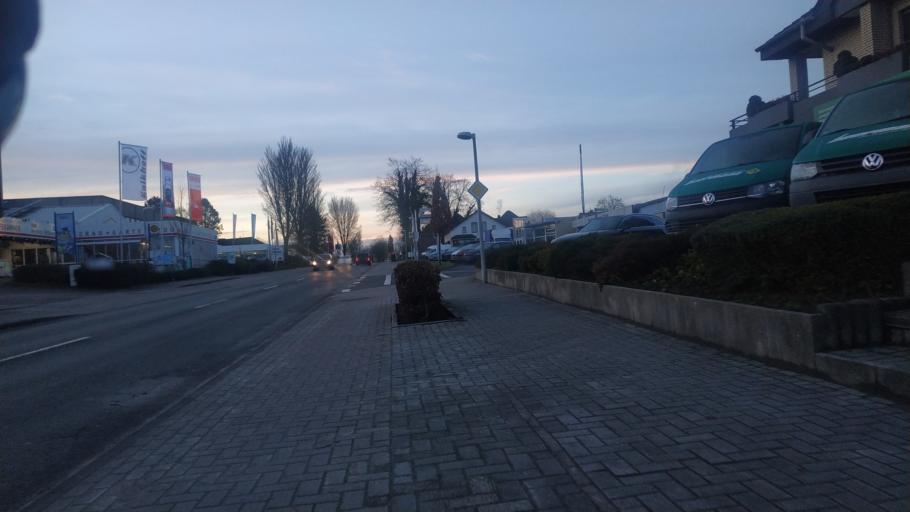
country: DE
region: North Rhine-Westphalia
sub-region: Regierungsbezirk Munster
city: Mettingen
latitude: 52.3199
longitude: 7.7752
